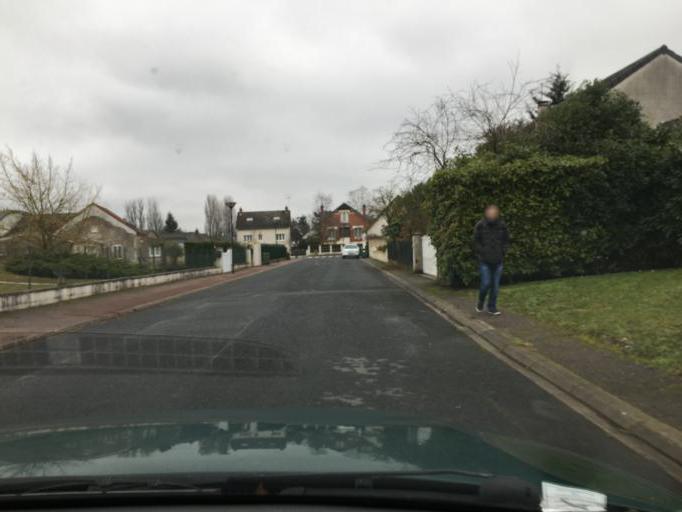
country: FR
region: Centre
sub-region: Departement du Loiret
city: Olivet
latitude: 47.8600
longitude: 1.8934
